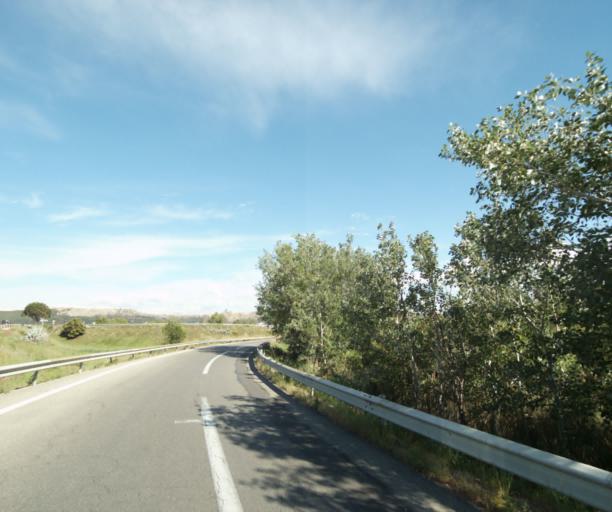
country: FR
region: Provence-Alpes-Cote d'Azur
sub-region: Departement des Bouches-du-Rhone
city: Rognac
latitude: 43.4932
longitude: 5.2152
